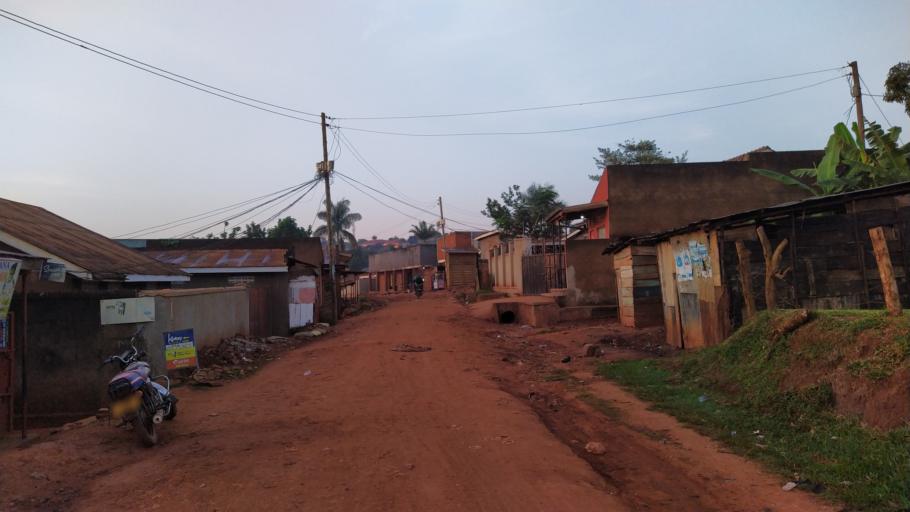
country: UG
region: Central Region
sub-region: Kampala District
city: Kampala
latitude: 0.2734
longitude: 32.5738
